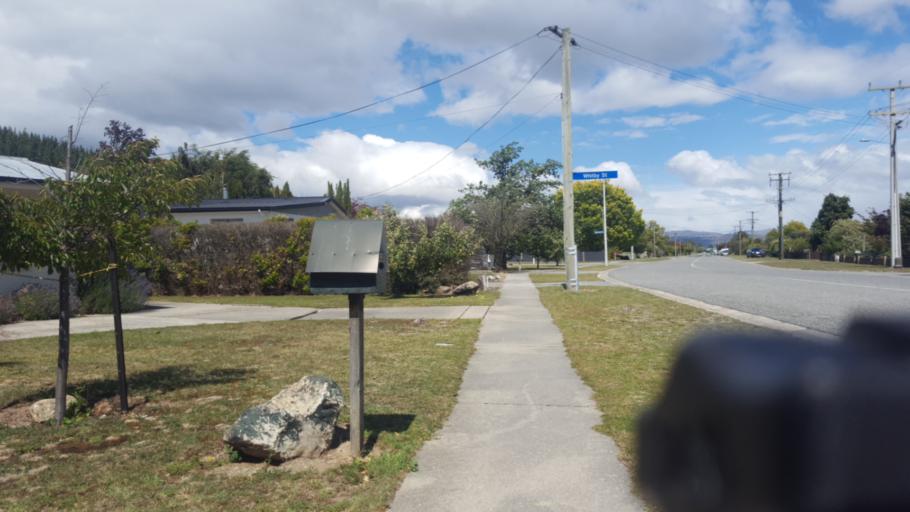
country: NZ
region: Otago
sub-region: Queenstown-Lakes District
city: Wanaka
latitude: -45.1879
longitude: 169.3241
